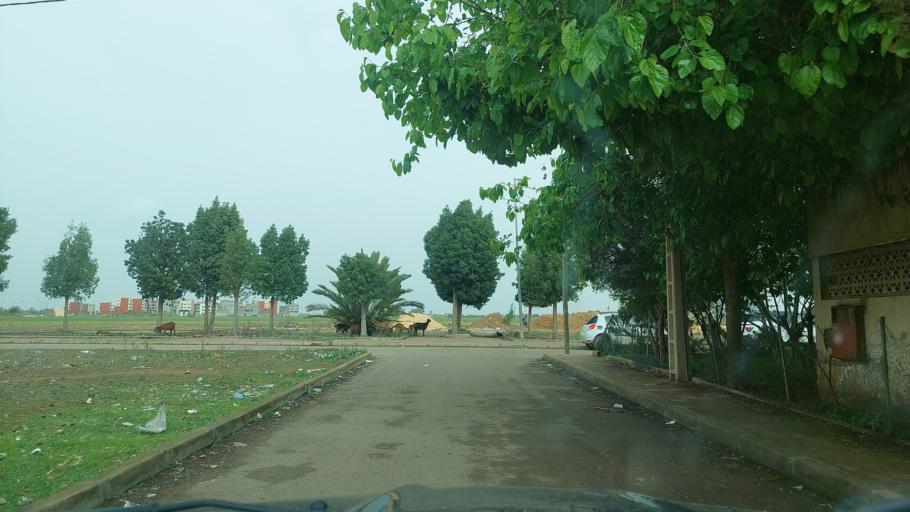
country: MA
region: Grand Casablanca
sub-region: Mediouna
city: Mediouna
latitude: 33.3726
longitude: -7.5268
